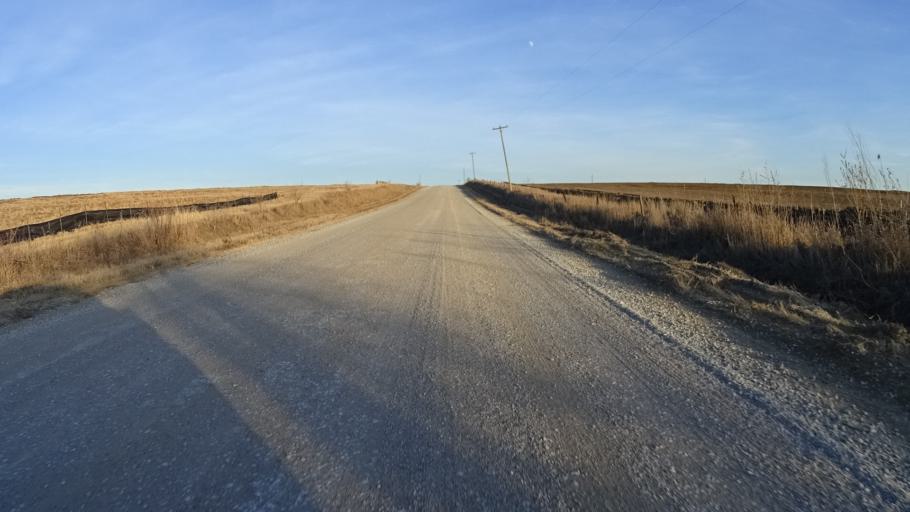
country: US
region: Nebraska
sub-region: Sarpy County
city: Papillion
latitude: 41.1326
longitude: -96.0974
